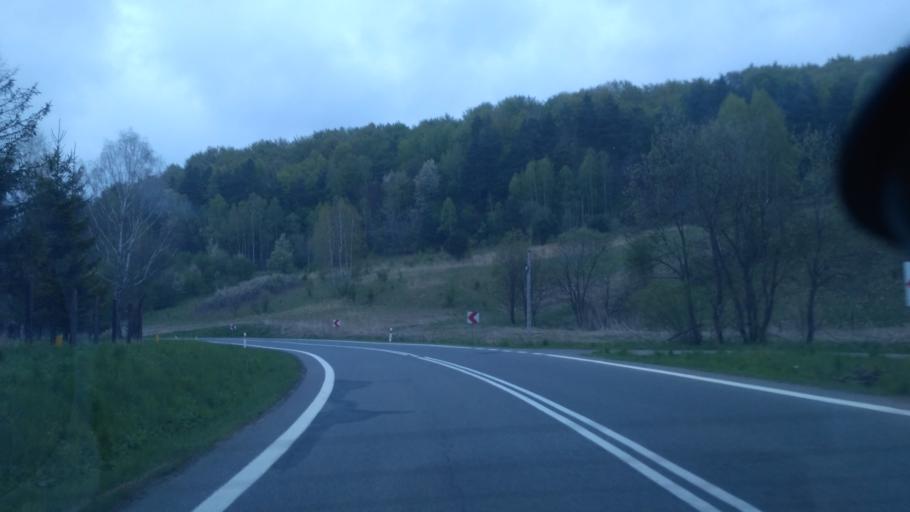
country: PL
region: Subcarpathian Voivodeship
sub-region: Powiat sanocki
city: Zagorz
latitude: 49.5378
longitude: 22.3037
